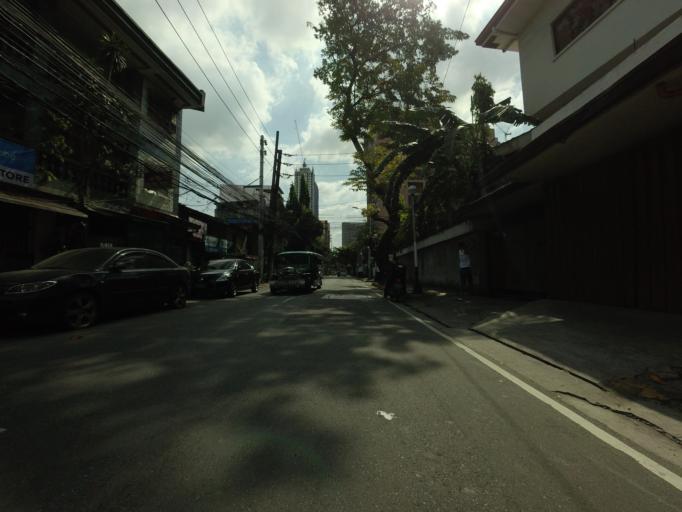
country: PH
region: Metro Manila
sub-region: City of Manila
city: Port Area
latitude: 14.5664
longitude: 120.9967
